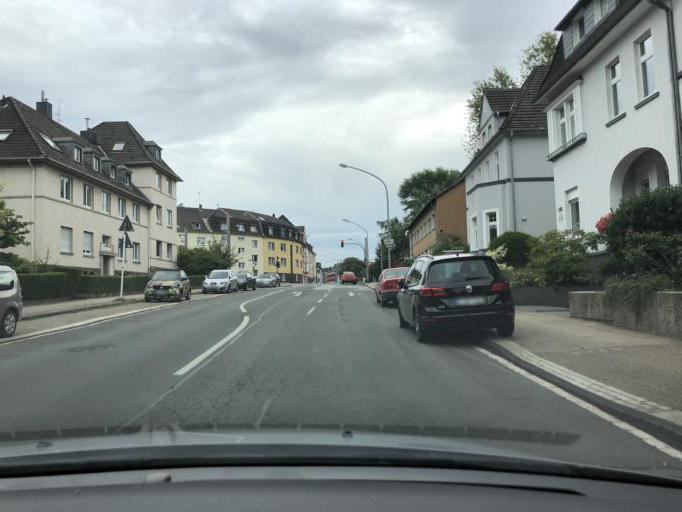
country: DE
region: North Rhine-Westphalia
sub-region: Regierungsbezirk Munster
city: Bottrop
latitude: 51.4676
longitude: 6.9439
